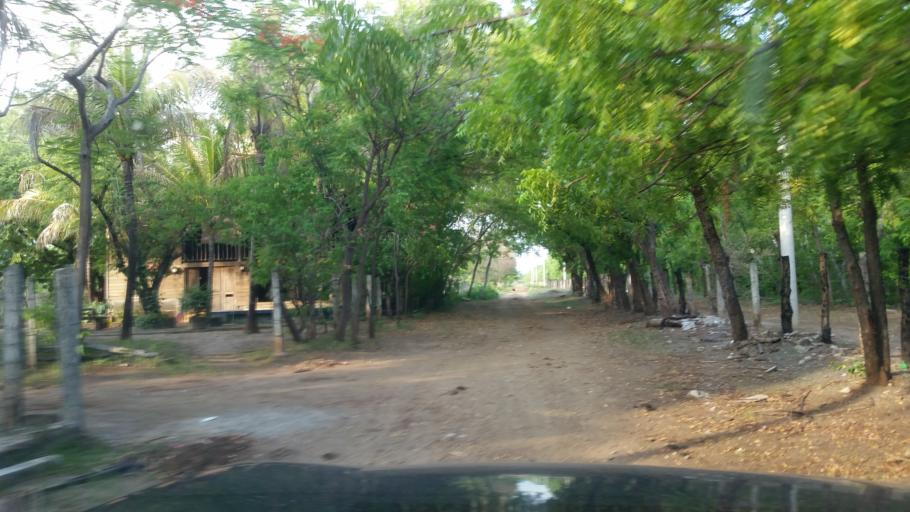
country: NI
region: Managua
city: Masachapa
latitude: 11.7642
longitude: -86.4967
